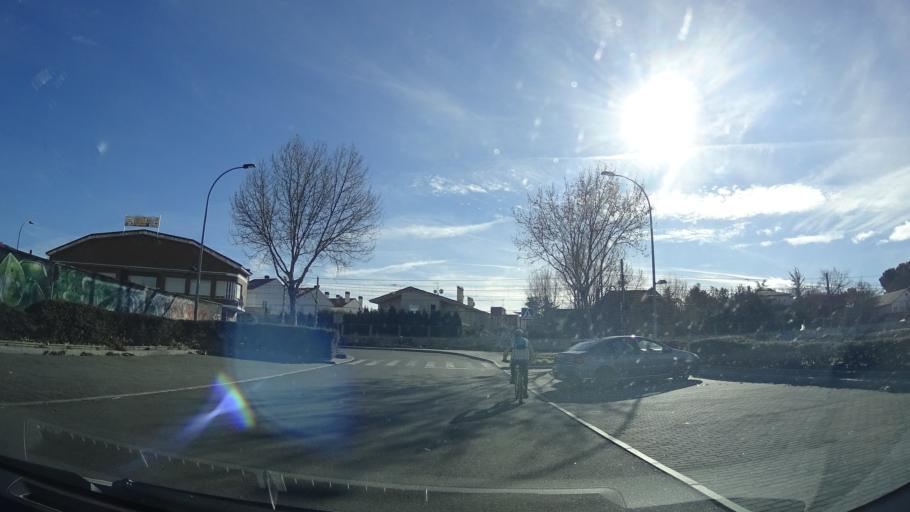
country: ES
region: Madrid
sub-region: Provincia de Madrid
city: Collado-Villalba
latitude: 40.6262
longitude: -4.0150
